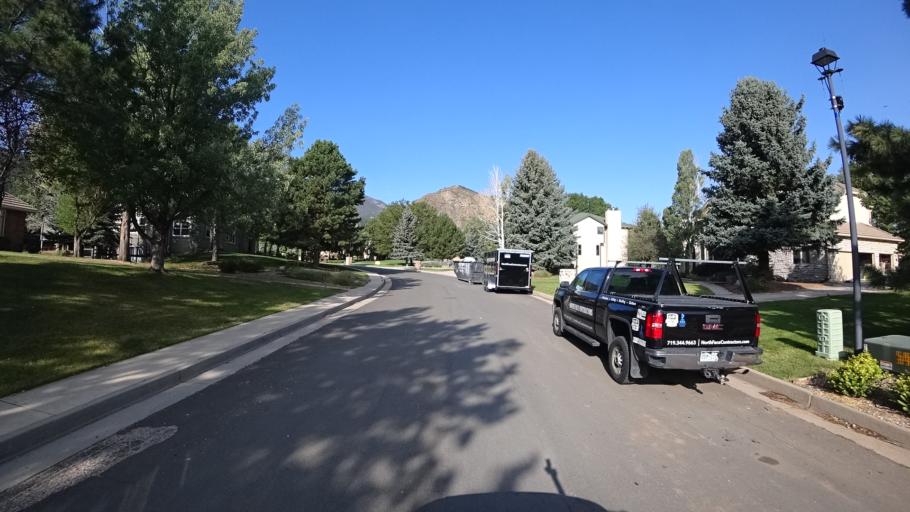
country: US
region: Colorado
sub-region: El Paso County
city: Manitou Springs
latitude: 38.8240
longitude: -104.8804
